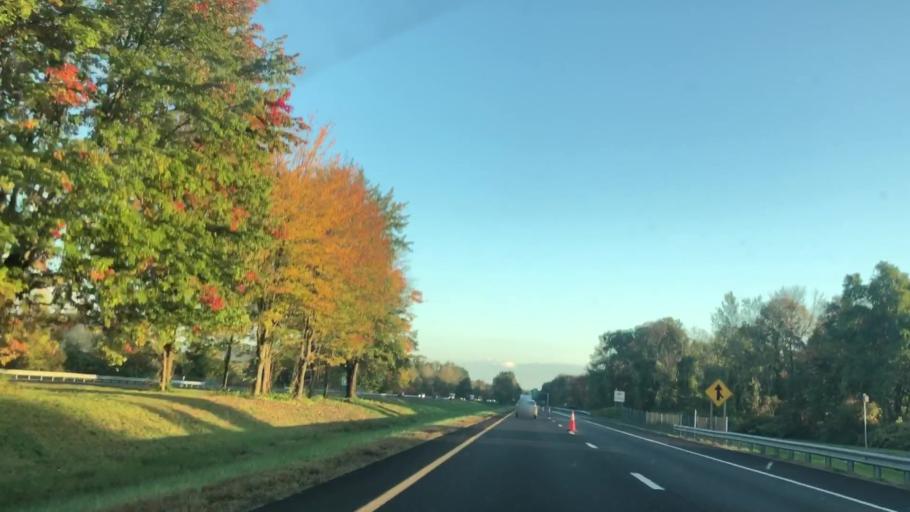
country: US
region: Massachusetts
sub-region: Franklin County
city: South Deerfield
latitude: 42.5050
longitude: -72.6204
